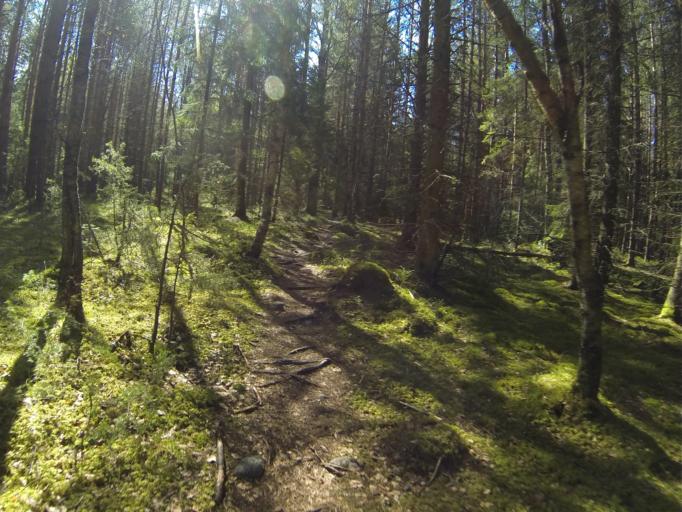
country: FI
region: Varsinais-Suomi
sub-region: Salo
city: Pertteli
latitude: 60.3916
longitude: 23.2108
